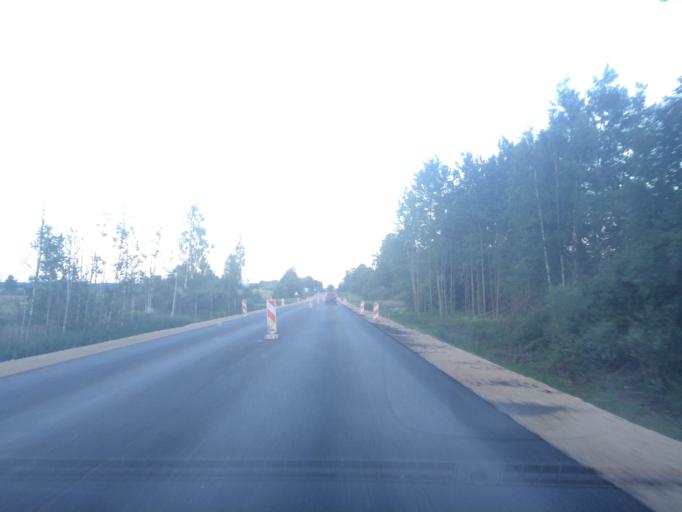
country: LT
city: Zarasai
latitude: 55.7498
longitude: 26.3174
